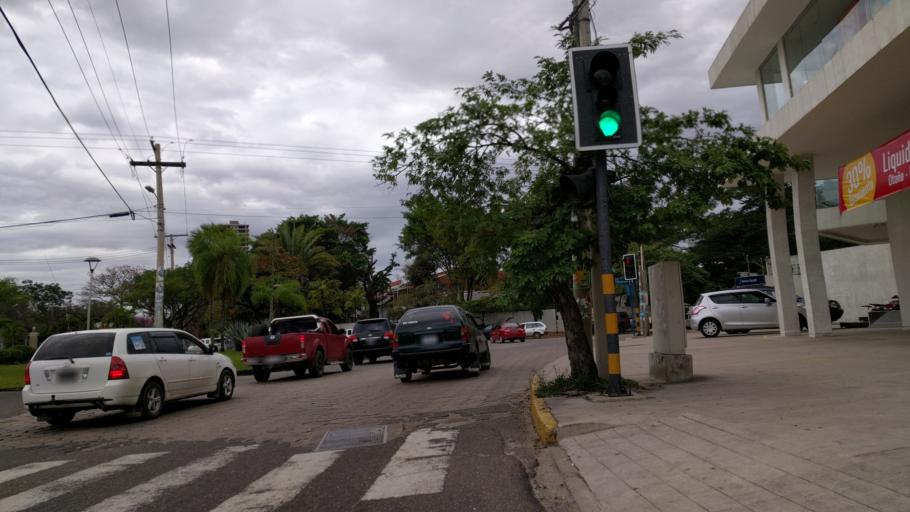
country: BO
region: Santa Cruz
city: Santa Cruz de la Sierra
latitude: -17.7630
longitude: -63.1972
